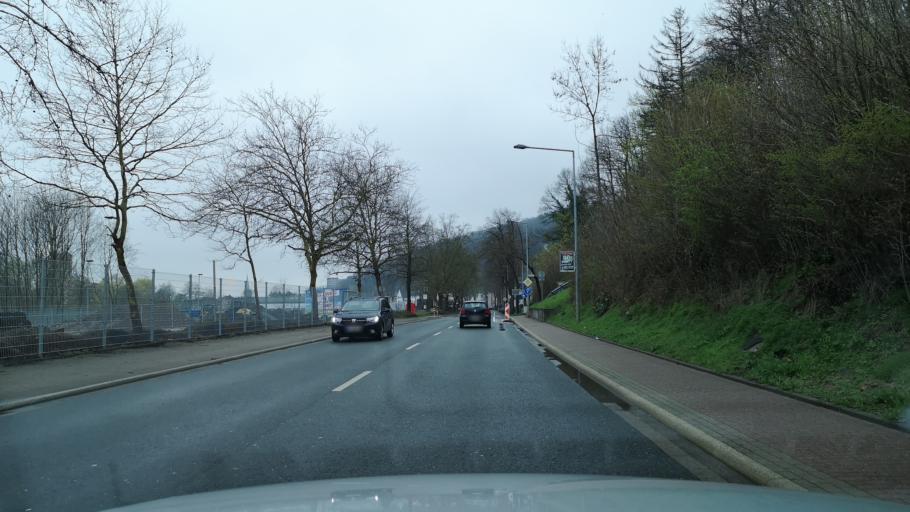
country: DE
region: North Rhine-Westphalia
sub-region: Regierungsbezirk Arnsberg
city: Menden
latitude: 51.4296
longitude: 7.8097
